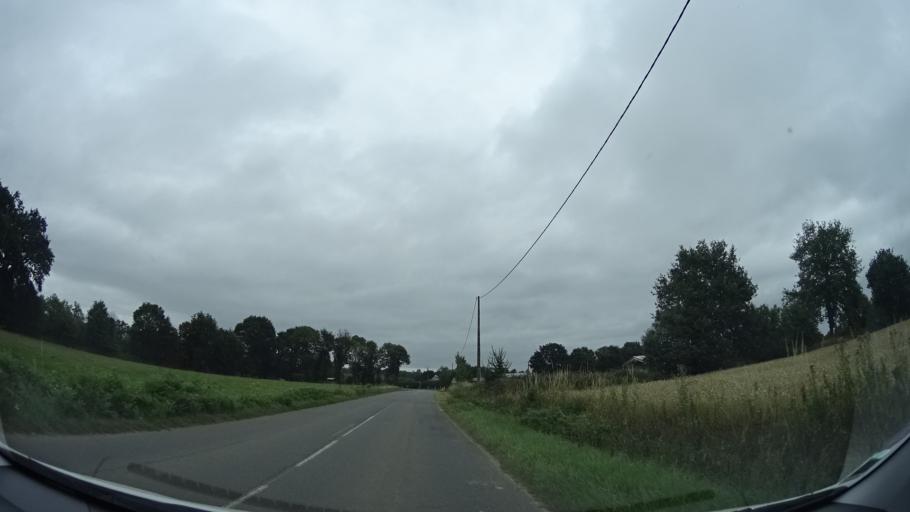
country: FR
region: Brittany
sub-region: Departement d'Ille-et-Vilaine
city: Quebriac
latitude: 48.3763
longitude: -1.8409
